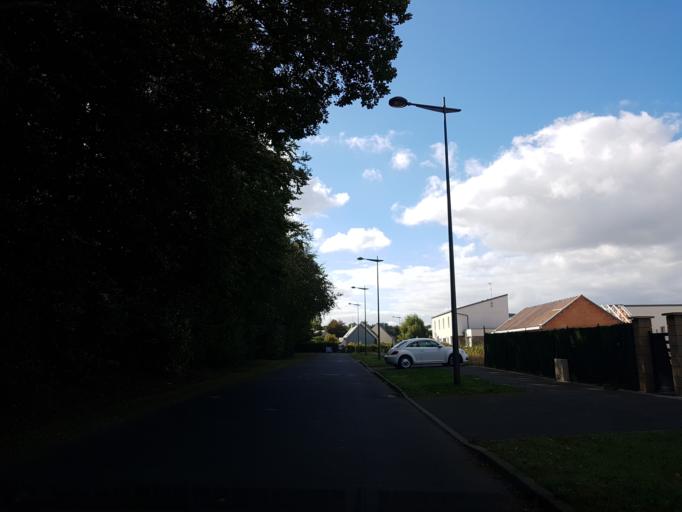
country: FR
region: Brittany
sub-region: Departement des Cotes-d'Armor
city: Pledran
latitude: 48.4606
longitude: -2.7391
